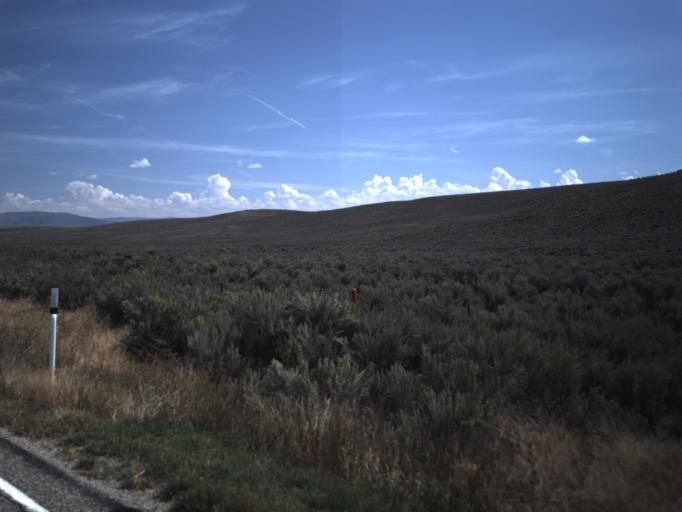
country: US
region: Utah
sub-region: Rich County
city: Randolph
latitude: 41.7695
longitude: -111.1543
